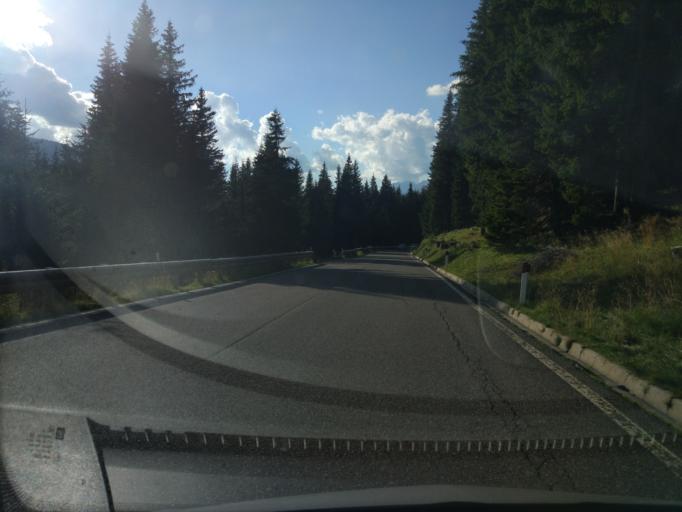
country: IT
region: Veneto
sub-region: Provincia di Belluno
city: Falcade Alto
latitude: 46.2944
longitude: 11.7724
